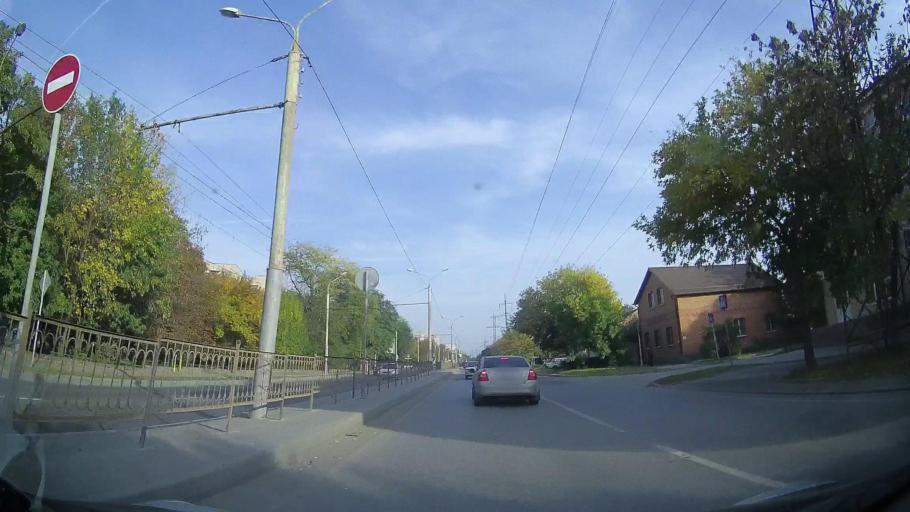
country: RU
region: Rostov
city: Imeni Chkalova
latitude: 47.2844
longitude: 39.7508
